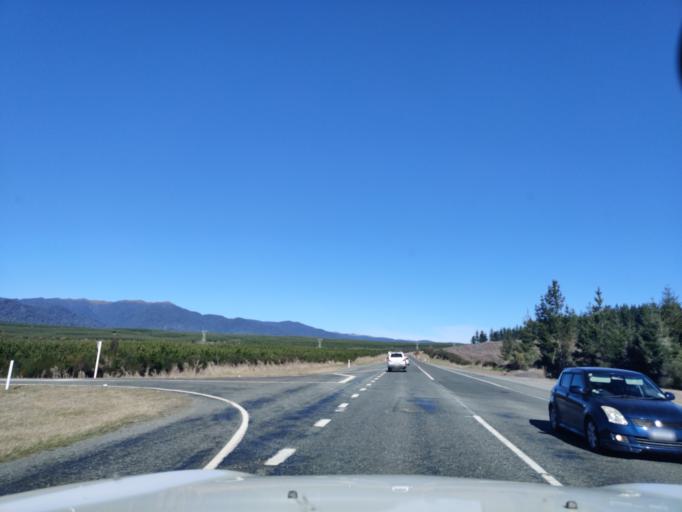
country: NZ
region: Waikato
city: Turangi
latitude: -39.0996
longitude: 175.8088
